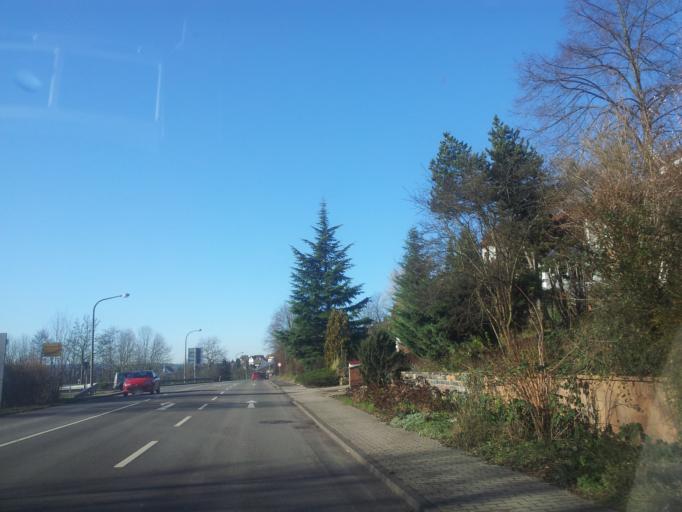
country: DE
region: Baden-Wuerttemberg
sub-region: Regierungsbezirk Stuttgart
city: Lehrensteinsfeld
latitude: 49.1363
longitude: 9.3745
